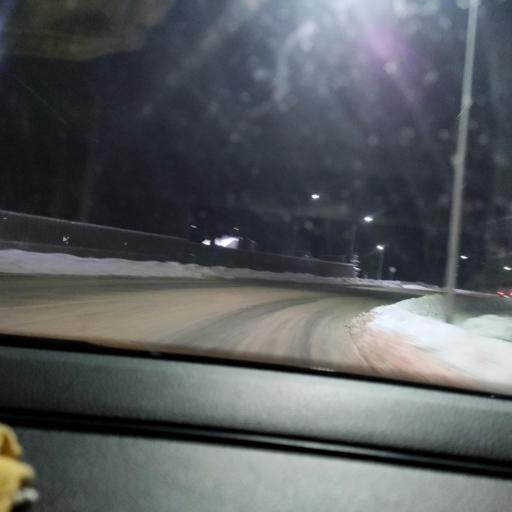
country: RU
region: Moskovskaya
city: Krasnogorsk
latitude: 55.8780
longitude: 37.3123
